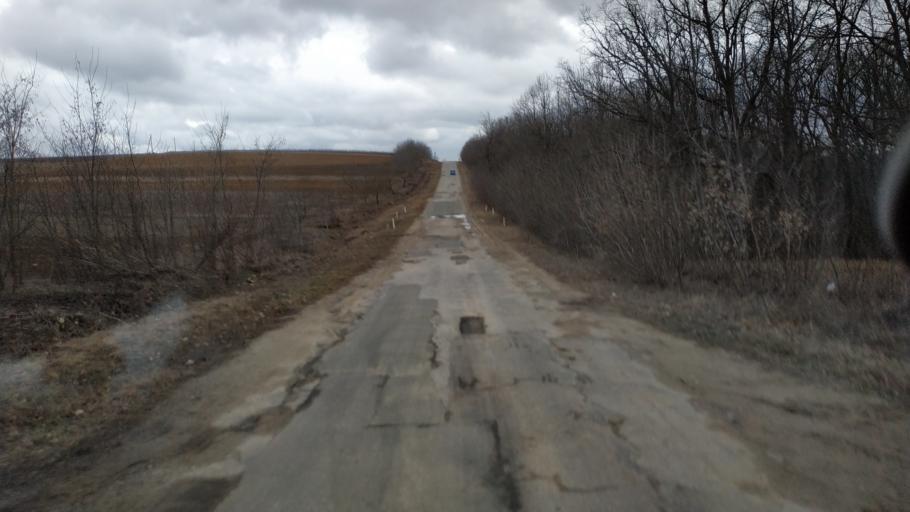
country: MD
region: Calarasi
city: Calarasi
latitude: 47.2264
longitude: 28.2476
